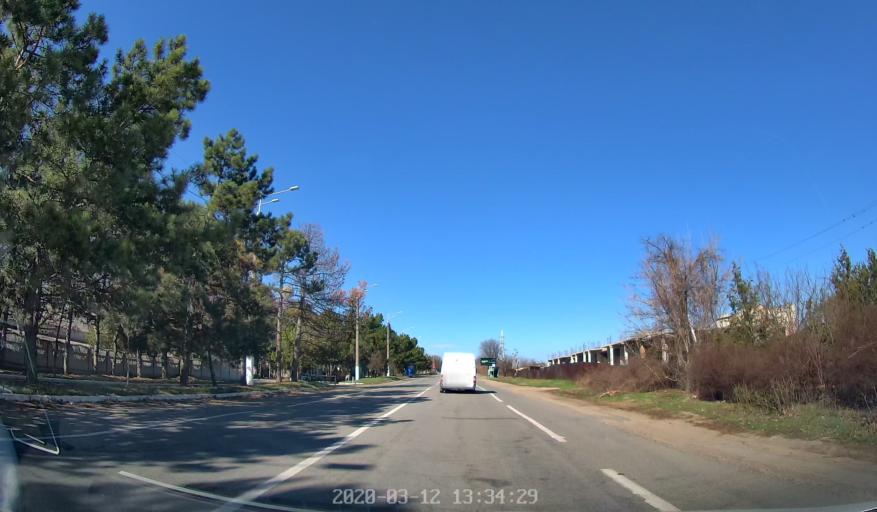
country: MD
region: Laloveni
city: Ialoveni
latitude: 46.9639
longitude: 28.7672
